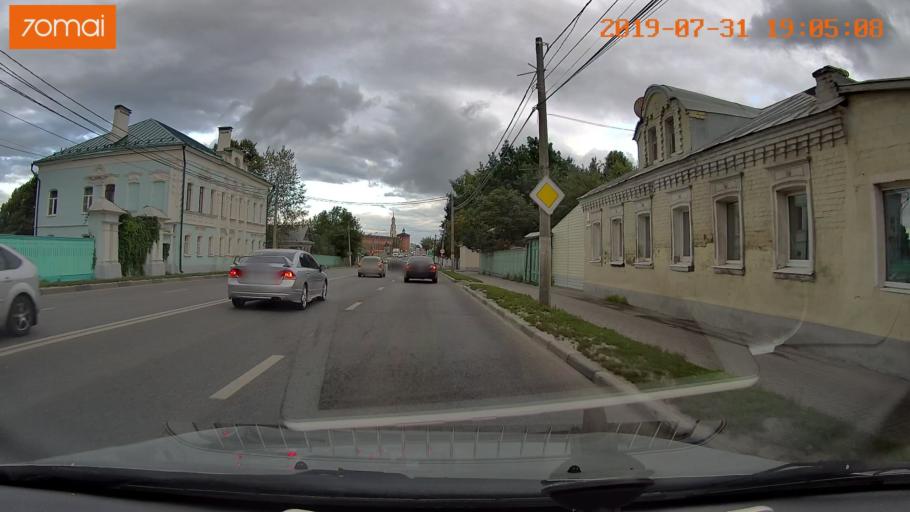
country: RU
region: Moskovskaya
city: Raduzhnyy
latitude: 55.1066
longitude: 38.7450
